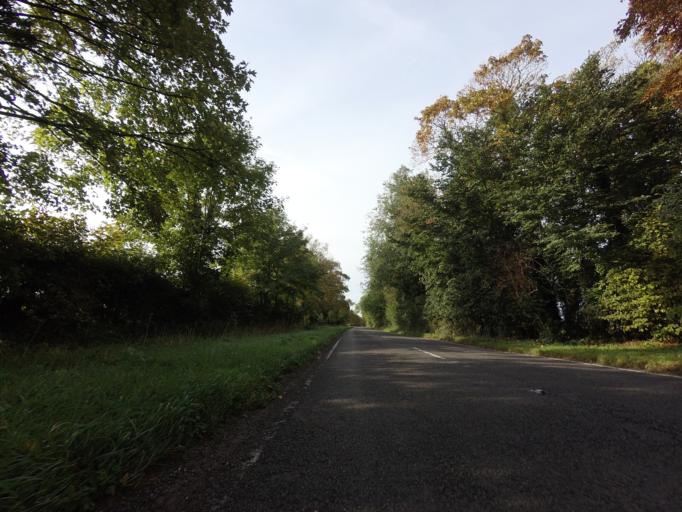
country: GB
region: England
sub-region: Cambridgeshire
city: Harston
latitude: 52.1143
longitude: 0.0954
